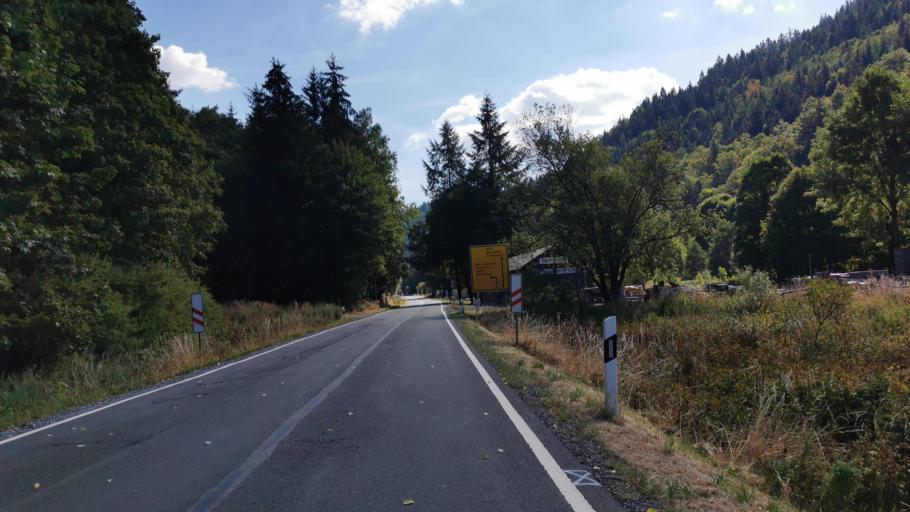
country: DE
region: Bavaria
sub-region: Upper Franconia
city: Nordhalben
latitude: 50.3574
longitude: 11.5159
